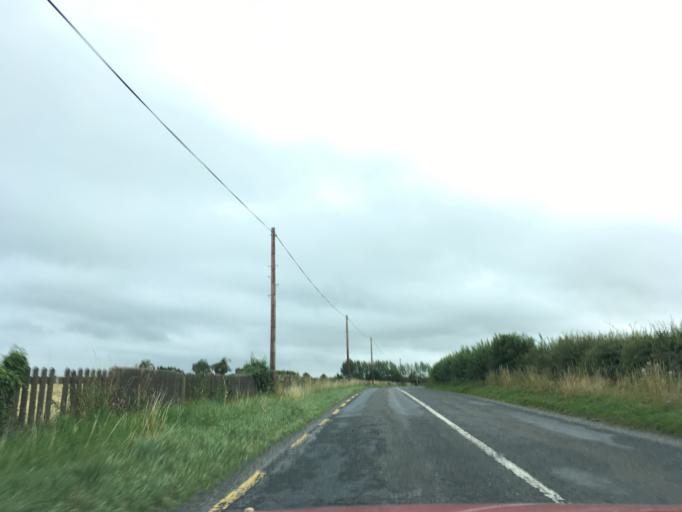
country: IE
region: Munster
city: Cashel
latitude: 52.4475
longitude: -7.8080
